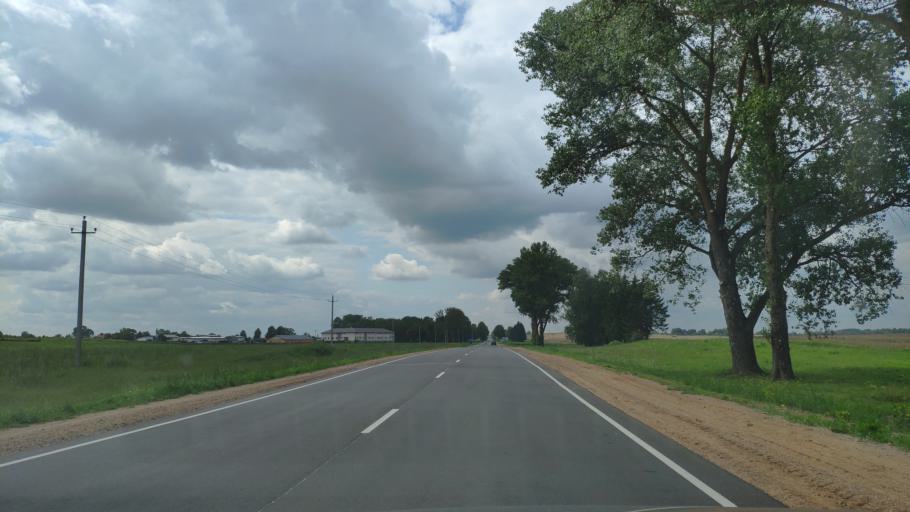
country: BY
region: Minsk
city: Zaslawye
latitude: 54.0058
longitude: 27.3405
